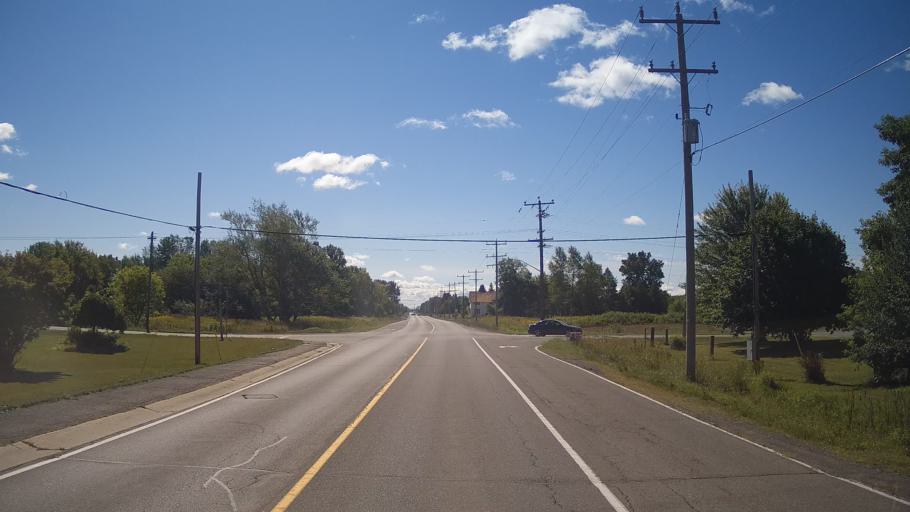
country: US
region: New York
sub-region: St. Lawrence County
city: Norfolk
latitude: 44.9354
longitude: -75.2127
